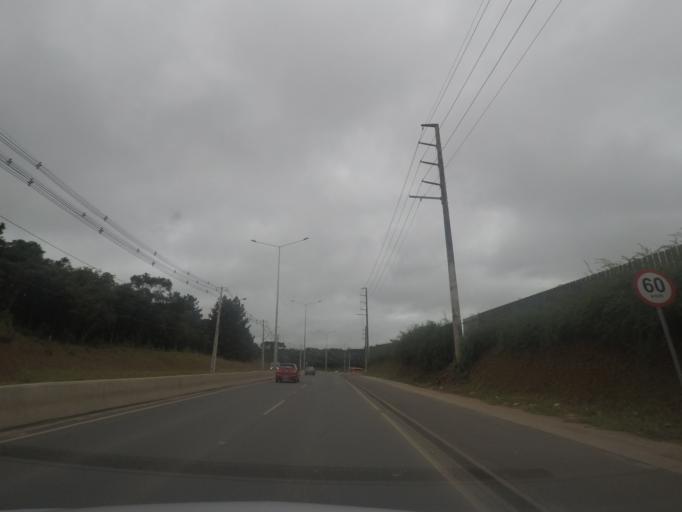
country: BR
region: Parana
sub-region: Piraquara
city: Piraquara
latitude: -25.4580
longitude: -49.0796
